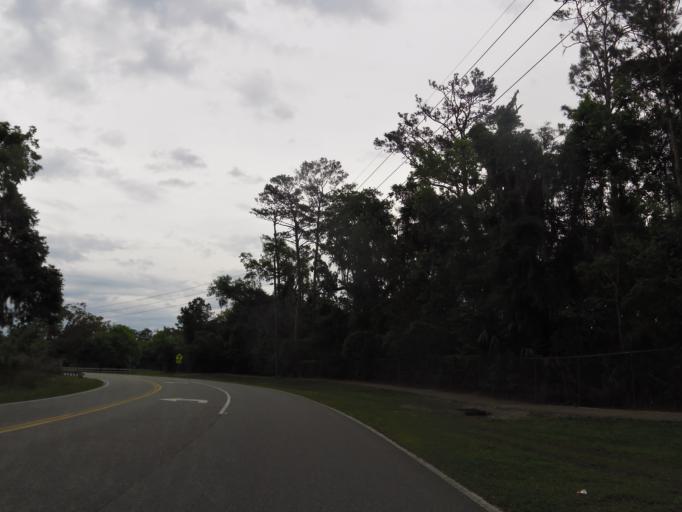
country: US
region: Florida
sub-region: Saint Johns County
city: Palm Valley
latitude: 30.1625
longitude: -81.3909
